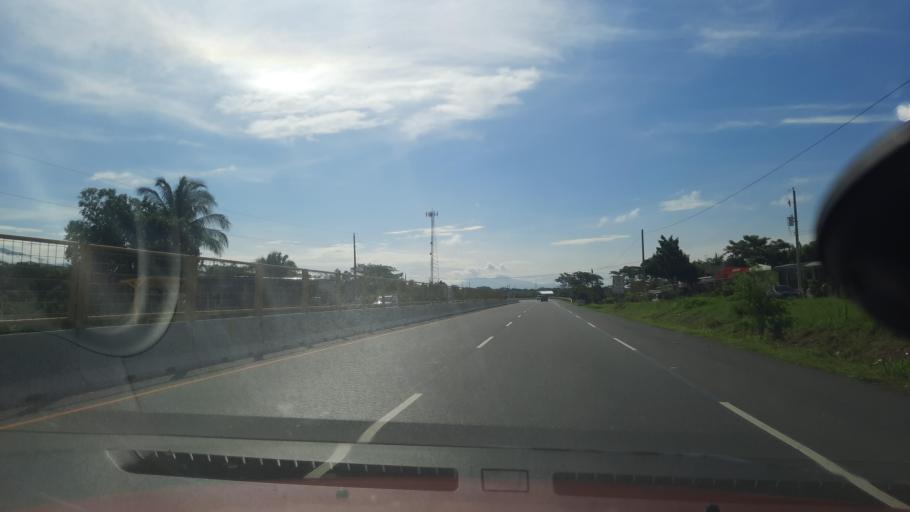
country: SV
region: La Paz
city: Santiago Nonualco
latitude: 13.4869
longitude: -88.9618
